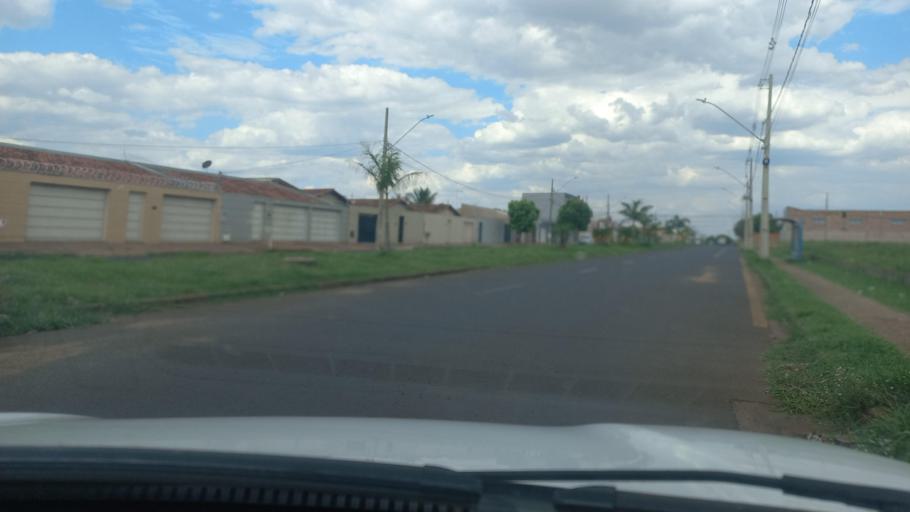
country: BR
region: Minas Gerais
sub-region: Uberaba
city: Uberaba
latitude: -19.7580
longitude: -47.9939
